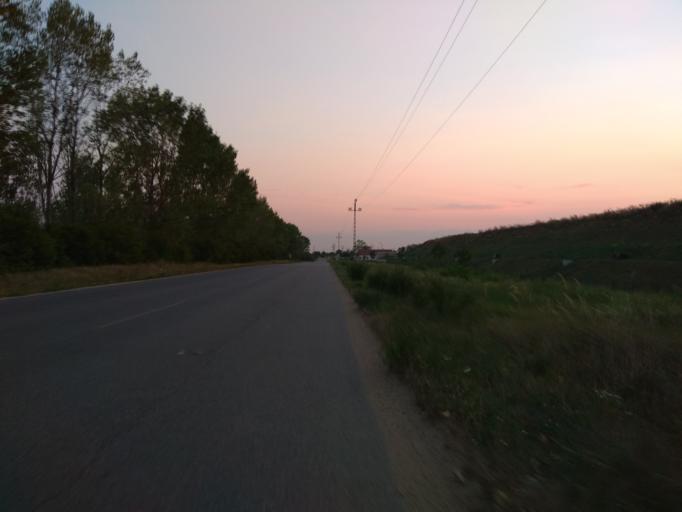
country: HU
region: Borsod-Abauj-Zemplen
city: Emod
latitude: 47.9144
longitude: 20.8699
